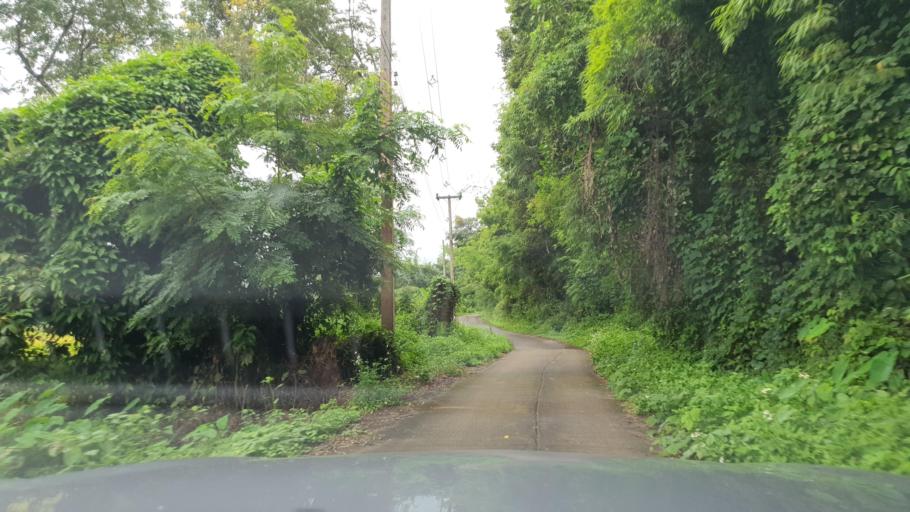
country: TH
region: Chiang Mai
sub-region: Amphoe Chiang Dao
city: Chiang Dao
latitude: 19.3370
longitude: 98.9272
